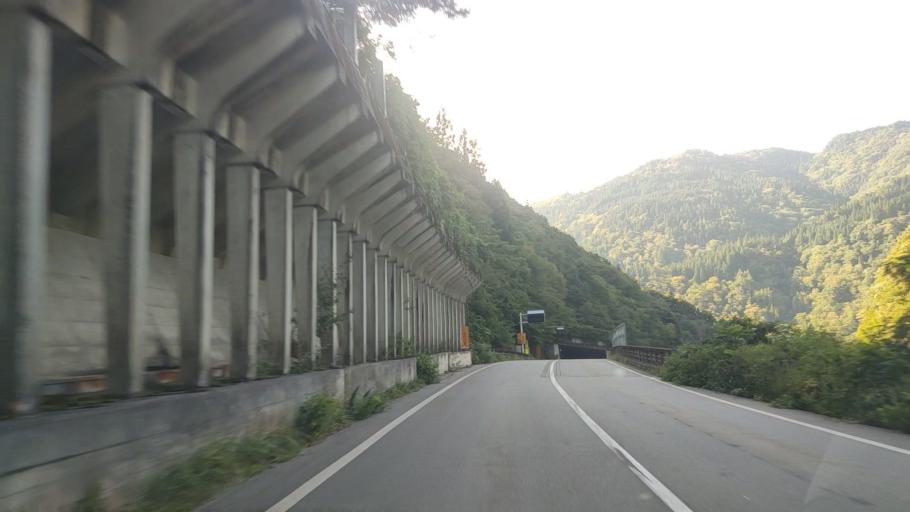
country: JP
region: Gifu
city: Takayama
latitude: 36.3114
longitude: 137.1267
